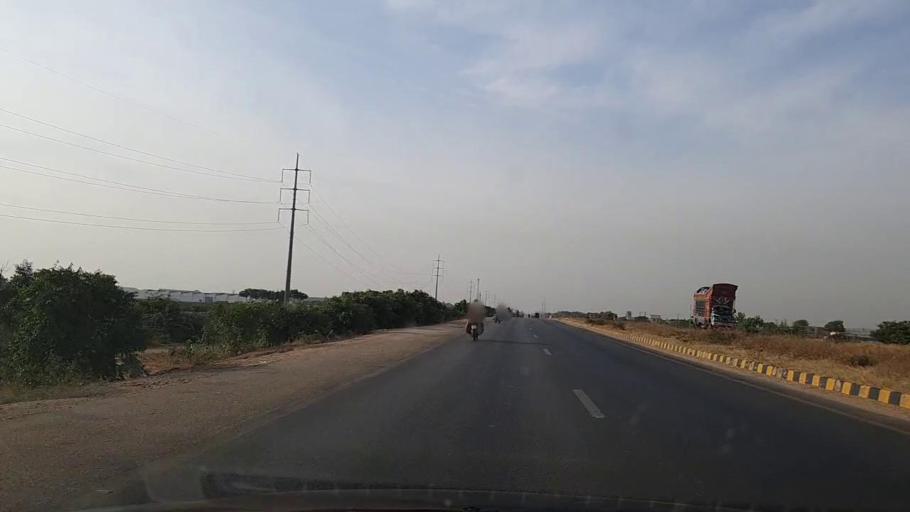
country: PK
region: Sindh
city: Gharo
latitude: 24.7751
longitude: 67.5424
